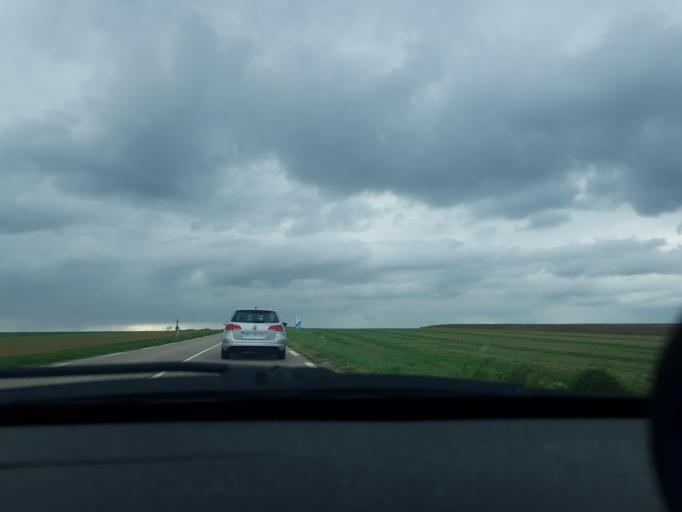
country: FR
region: Lorraine
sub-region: Departement de la Moselle
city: Faulquemont
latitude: 48.9963
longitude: 6.5971
